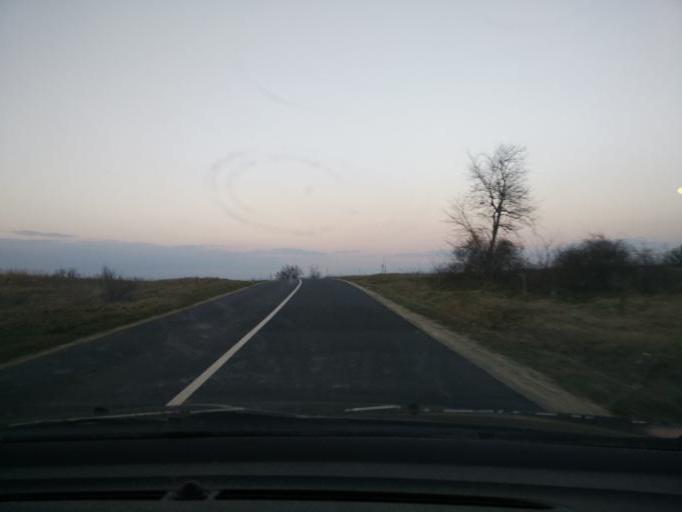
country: HU
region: Veszprem
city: Csabrendek
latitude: 47.0370
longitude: 17.3131
